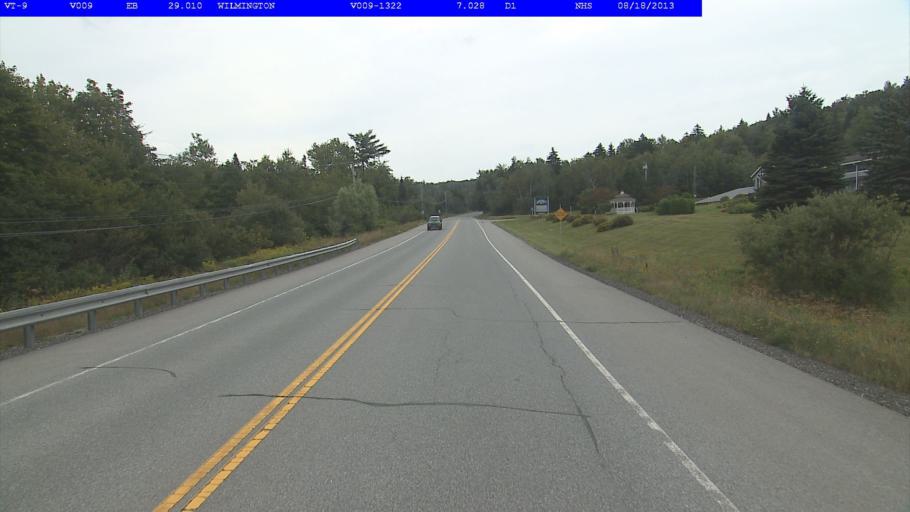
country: US
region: Vermont
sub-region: Windham County
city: Dover
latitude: 42.8594
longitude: -72.8045
